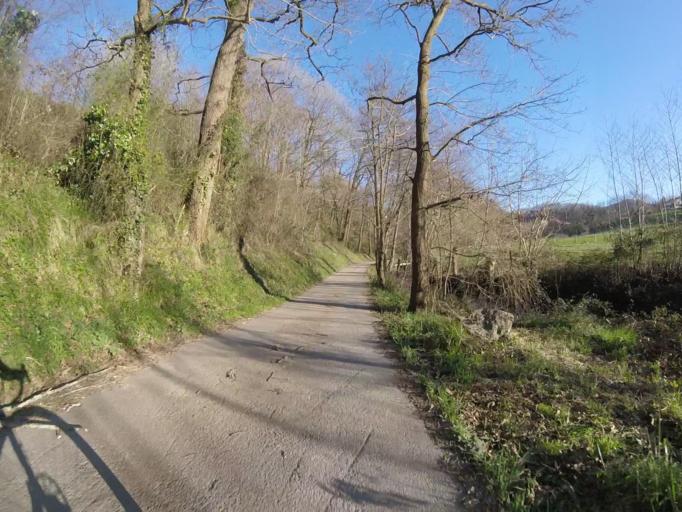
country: ES
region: Basque Country
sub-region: Provincia de Guipuzcoa
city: Errenteria
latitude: 43.2894
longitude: -1.8731
